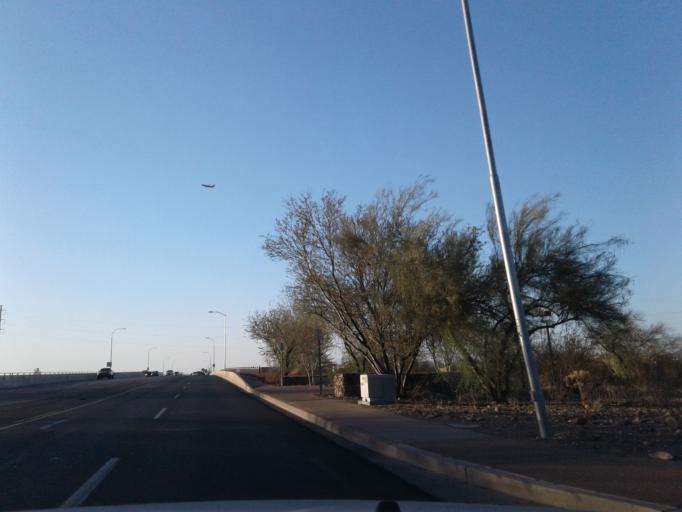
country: US
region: Arizona
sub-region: Maricopa County
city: Phoenix
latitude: 33.4161
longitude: -112.0472
